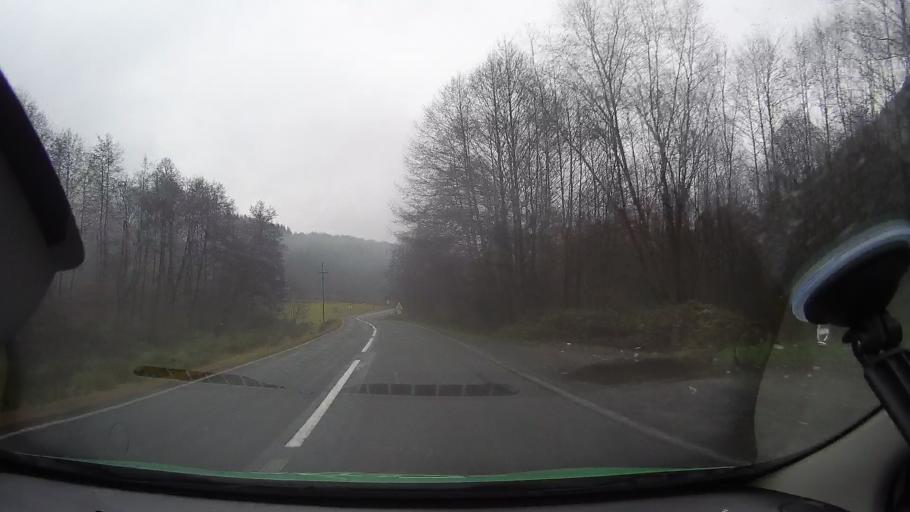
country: RO
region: Arad
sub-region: Comuna Plescuta
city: Plescuta
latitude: 46.3140
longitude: 22.4565
